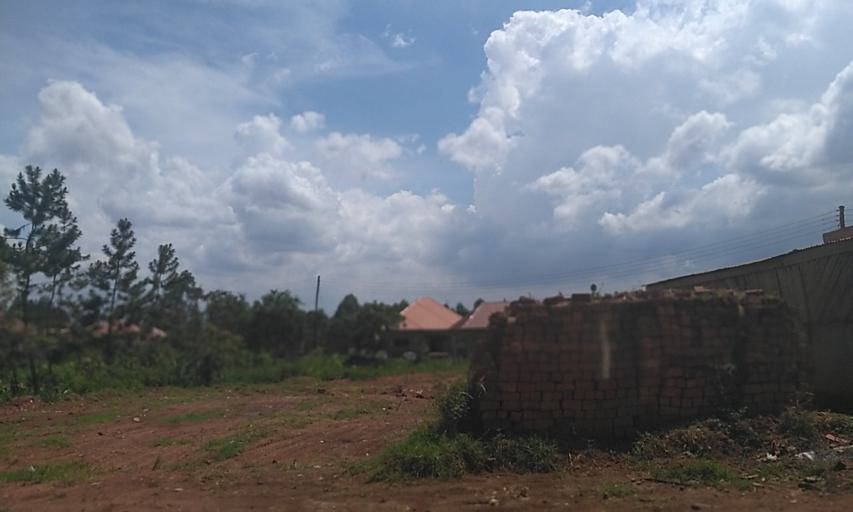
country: UG
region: Central Region
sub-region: Wakiso District
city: Wakiso
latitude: 0.4050
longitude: 32.4904
